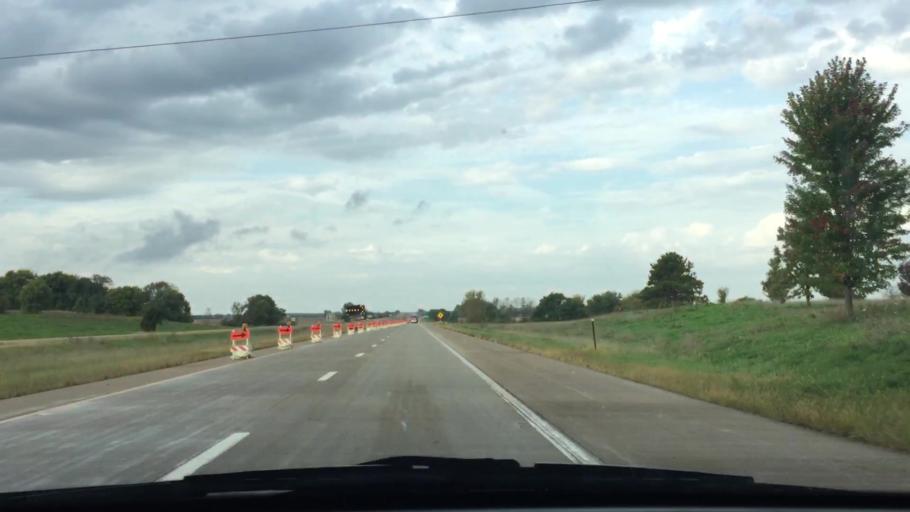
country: US
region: Illinois
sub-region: Whiteside County
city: Prophetstown
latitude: 41.7224
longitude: -89.9674
